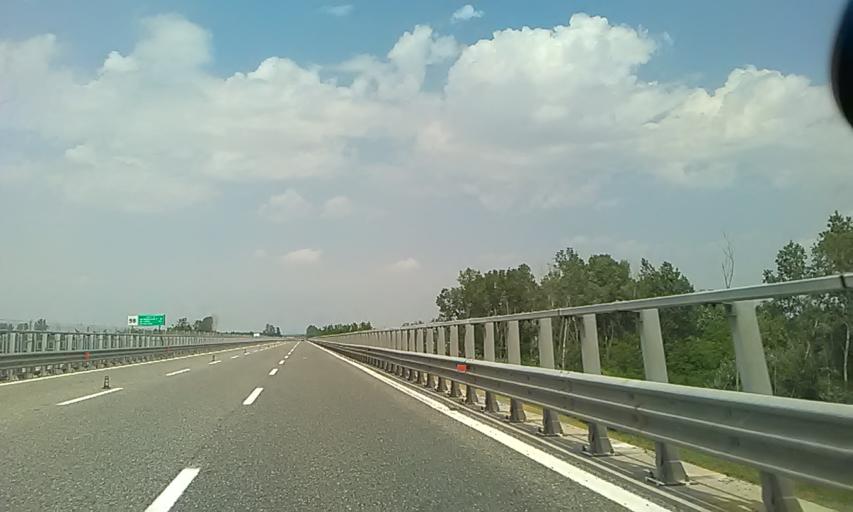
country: IT
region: Piedmont
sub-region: Provincia di Alessandria
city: Castellazzo Bormida
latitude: 44.8617
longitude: 8.5826
